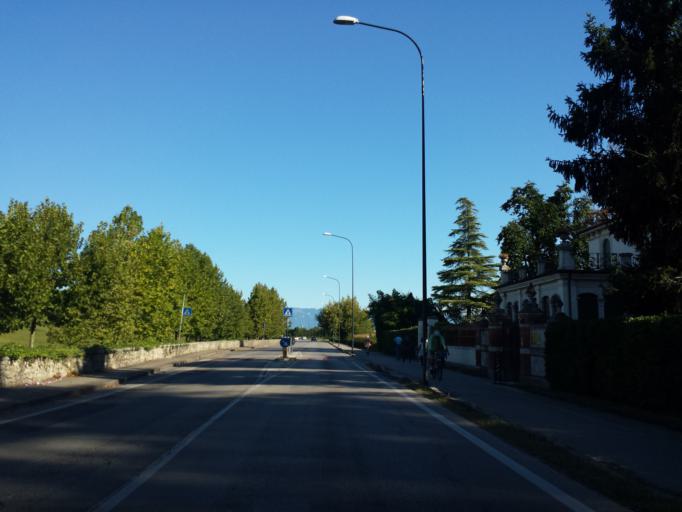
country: IT
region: Veneto
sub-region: Provincia di Vicenza
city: Vicenza
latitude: 45.5292
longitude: 11.5630
